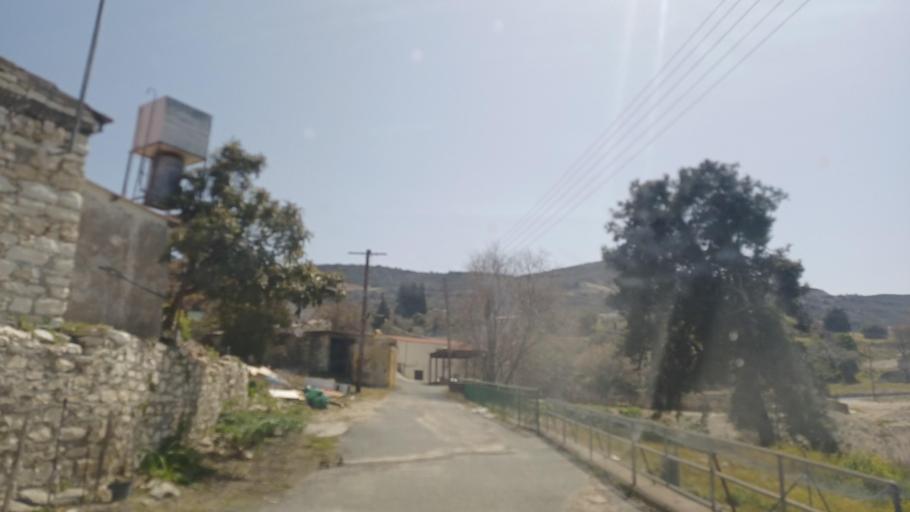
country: CY
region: Limassol
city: Pachna
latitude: 34.8628
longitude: 32.7525
